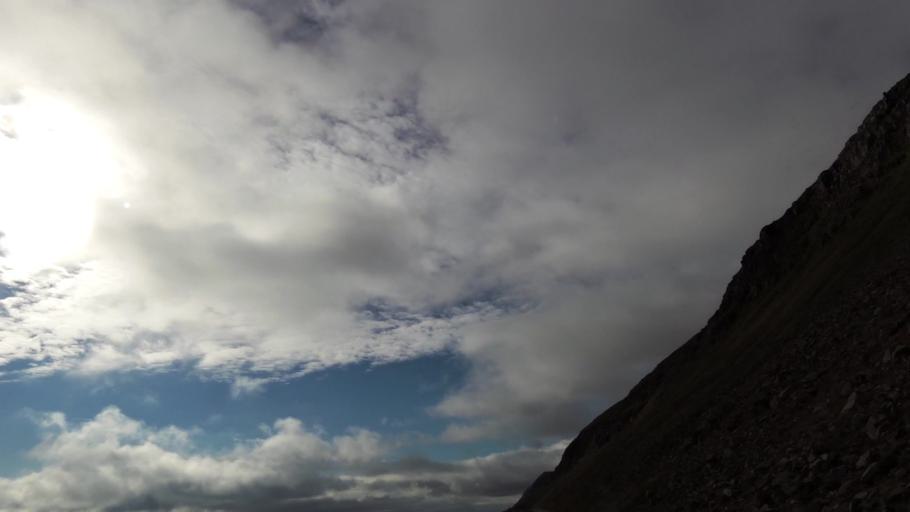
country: IS
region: West
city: Olafsvik
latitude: 65.5656
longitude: -23.9208
